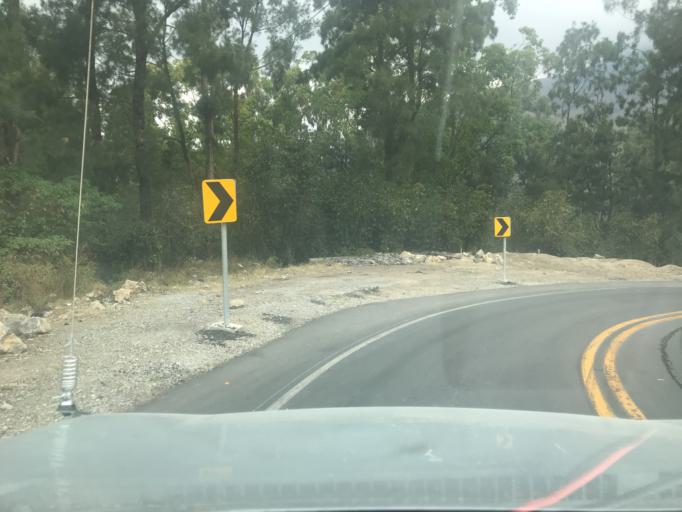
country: TL
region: Manufahi
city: Same
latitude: -8.8855
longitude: 125.6040
